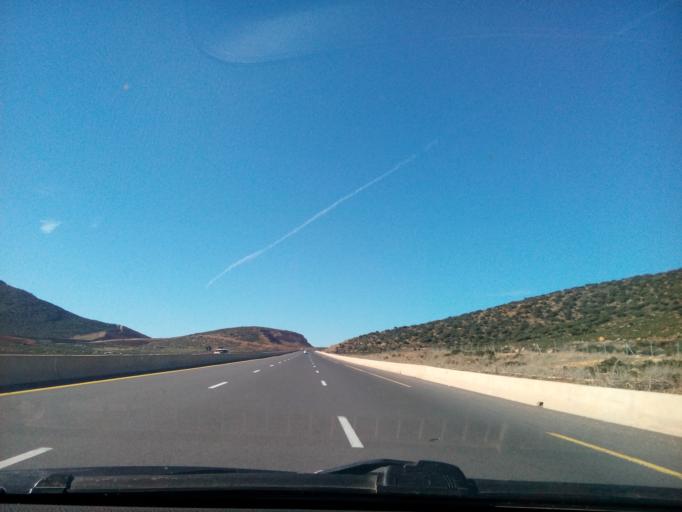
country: DZ
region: Tlemcen
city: Sidi Abdelli
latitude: 35.0203
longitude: -1.1271
